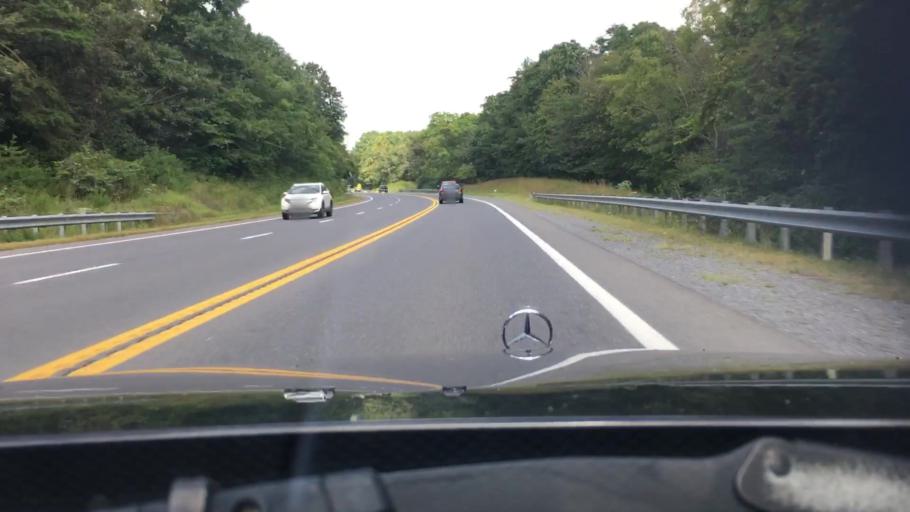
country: US
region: Maryland
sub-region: Washington County
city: Hancock
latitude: 39.6828
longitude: -78.1910
